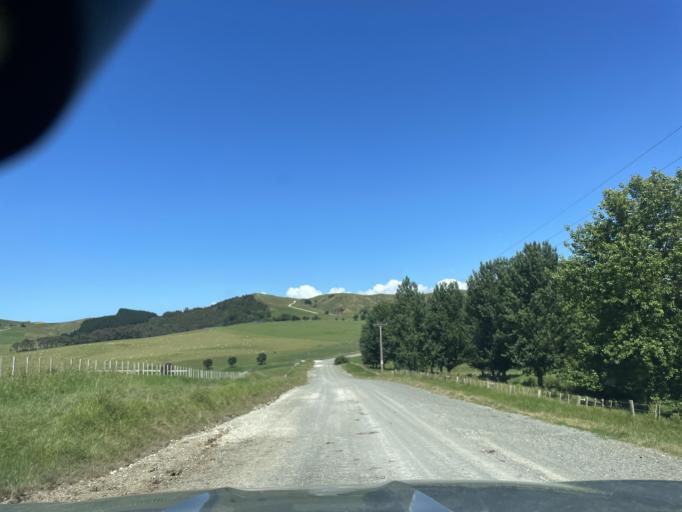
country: NZ
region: Auckland
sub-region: Auckland
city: Wellsford
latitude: -36.2885
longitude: 174.3356
